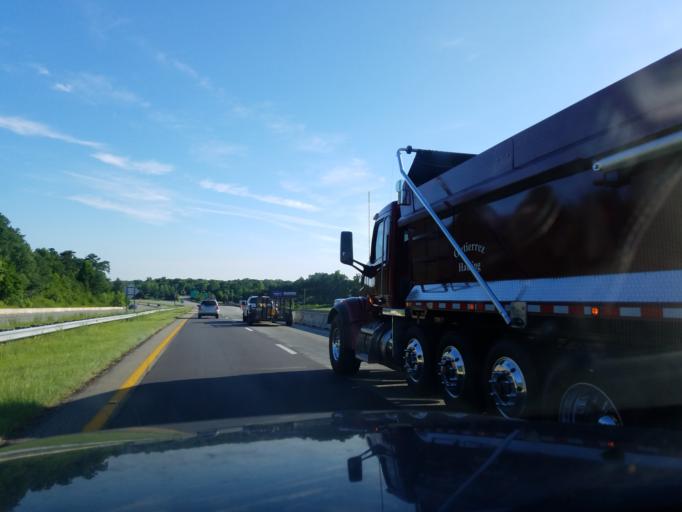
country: US
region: North Carolina
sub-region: Durham County
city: Durham
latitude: 35.9990
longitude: -78.8631
